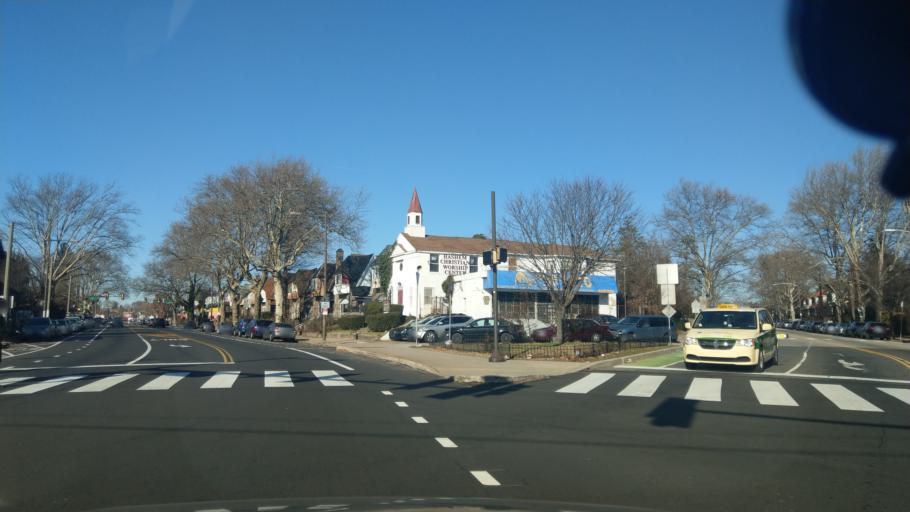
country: US
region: Pennsylvania
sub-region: Montgomery County
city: Wyncote
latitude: 40.0584
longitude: -75.1492
